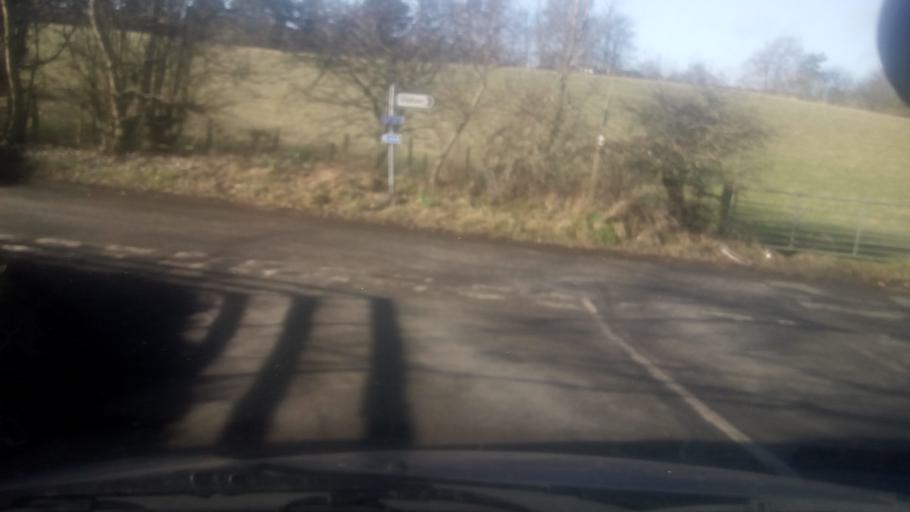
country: GB
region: Scotland
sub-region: The Scottish Borders
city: Jedburgh
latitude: 55.4868
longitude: -2.5414
